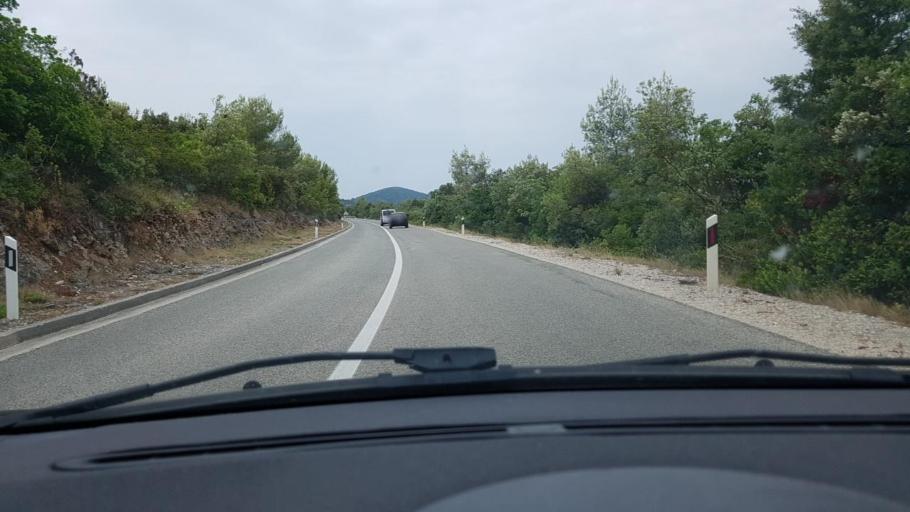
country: HR
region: Dubrovacko-Neretvanska
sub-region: Grad Korcula
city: Zrnovo
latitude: 42.9383
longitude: 17.0785
